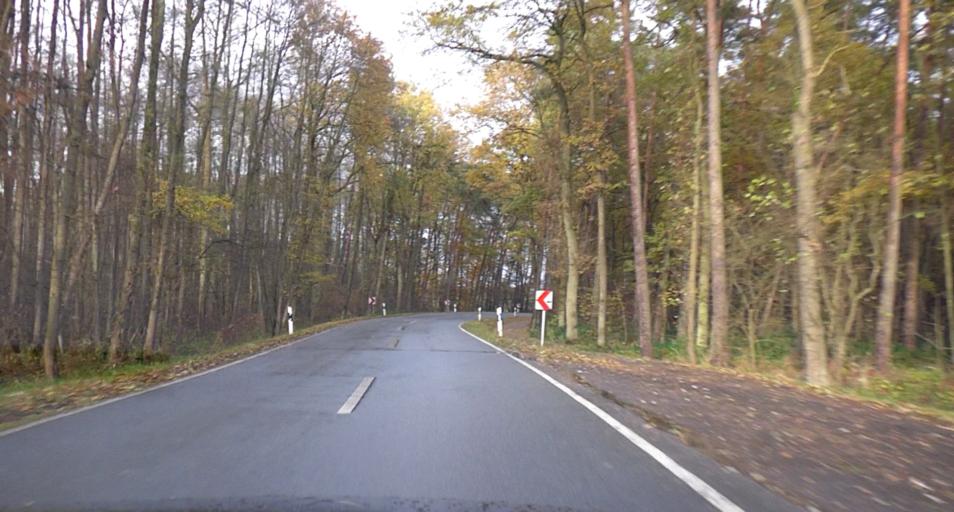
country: DE
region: Bavaria
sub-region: Upper Franconia
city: Langensendelbach
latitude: 49.6378
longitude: 11.0539
